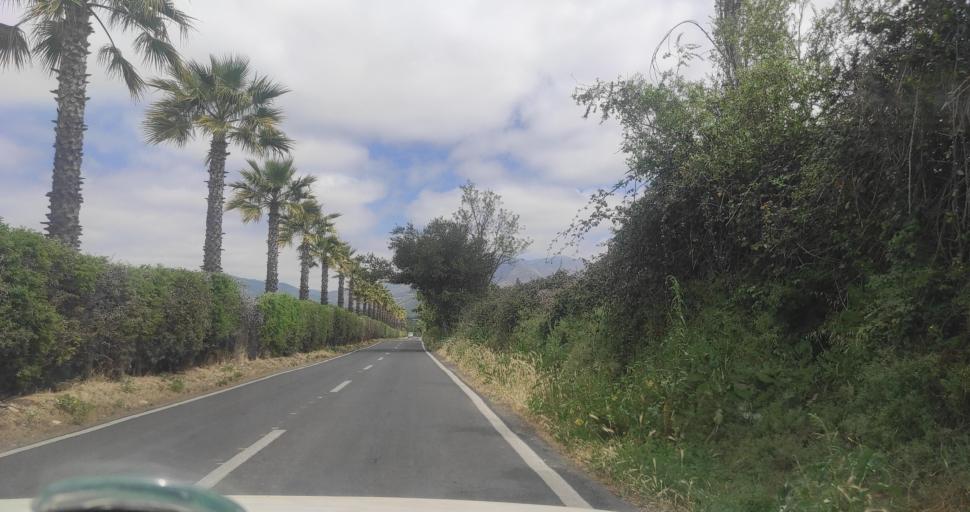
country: CL
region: Valparaiso
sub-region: Provincia de Marga Marga
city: Limache
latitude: -33.0292
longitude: -71.2300
